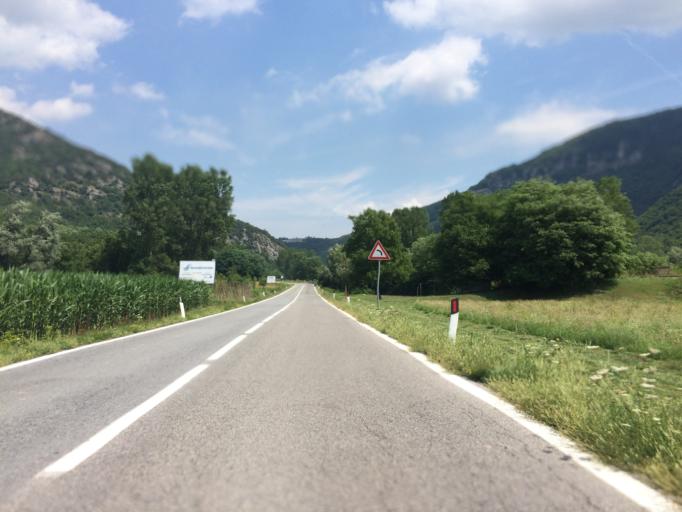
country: IT
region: Piedmont
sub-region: Provincia di Cuneo
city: Priola
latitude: 44.2673
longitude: 8.0284
